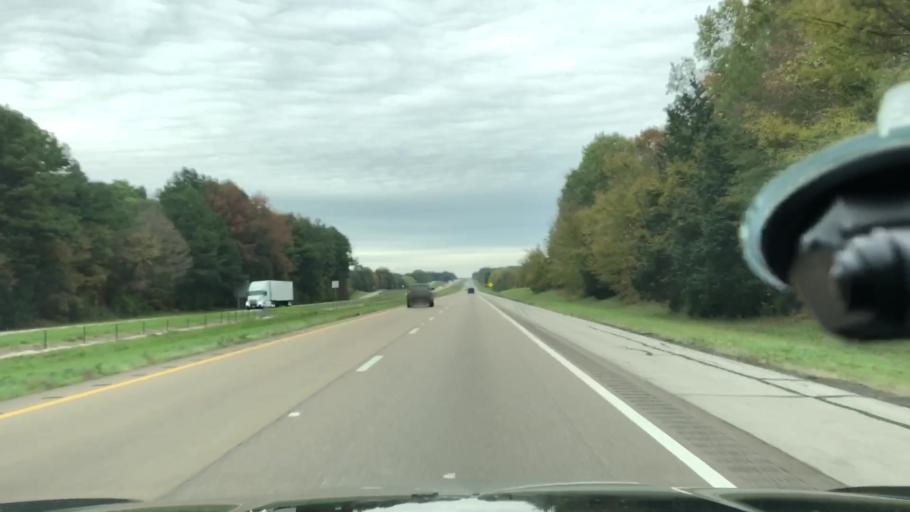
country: US
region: Texas
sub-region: Morris County
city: Omaha
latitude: 33.2538
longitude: -94.8438
